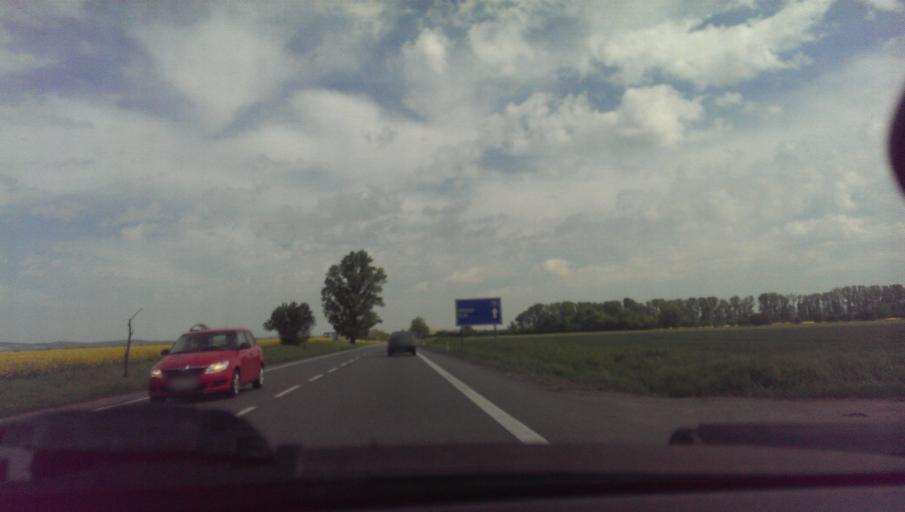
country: CZ
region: Zlin
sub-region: Okres Uherske Hradiste
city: Uherske Hradiste
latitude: 49.0928
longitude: 17.4519
